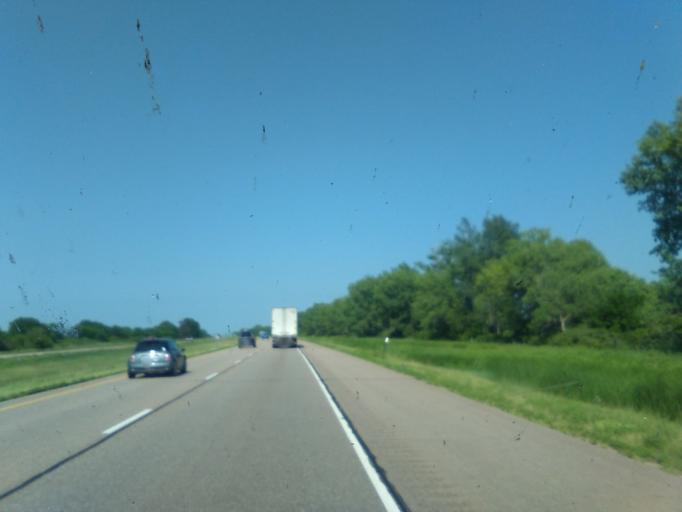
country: US
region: Nebraska
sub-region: Buffalo County
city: Shelton
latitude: 40.7268
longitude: -98.6702
